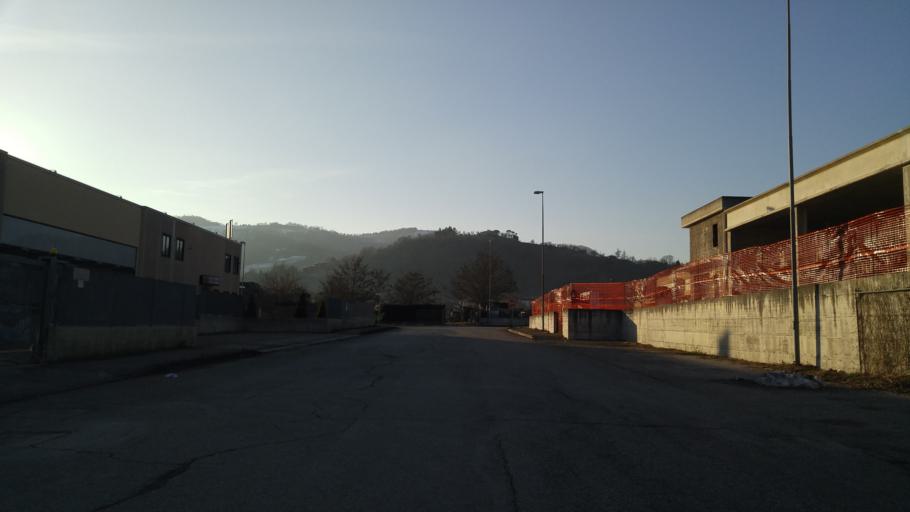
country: IT
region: The Marches
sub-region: Provincia di Pesaro e Urbino
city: Fermignano
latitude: 43.6886
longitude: 12.6476
